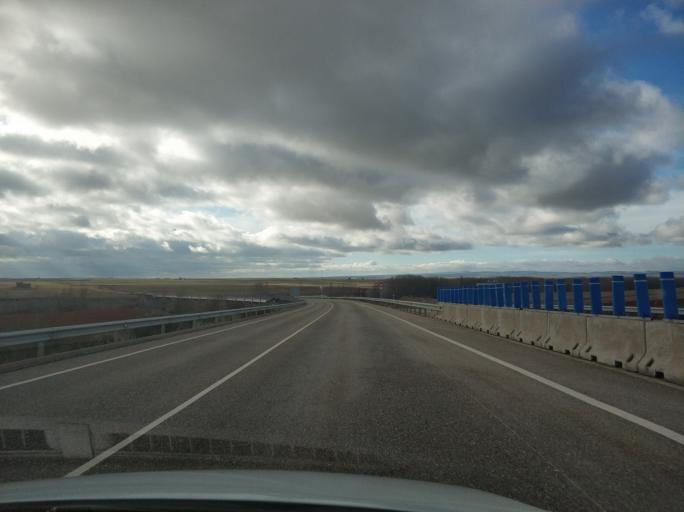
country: ES
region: Castille and Leon
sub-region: Provincia de Segovia
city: Ayllon
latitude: 41.4297
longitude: -3.3812
